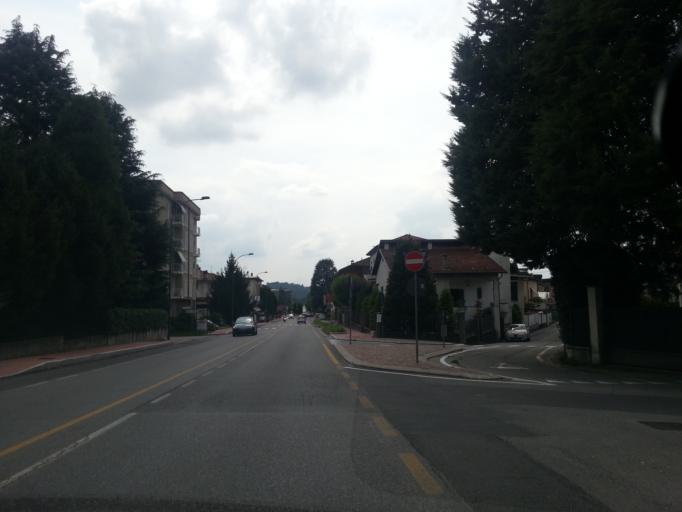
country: IT
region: Lombardy
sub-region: Provincia di Lecco
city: Oggiono
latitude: 45.7899
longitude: 9.3508
